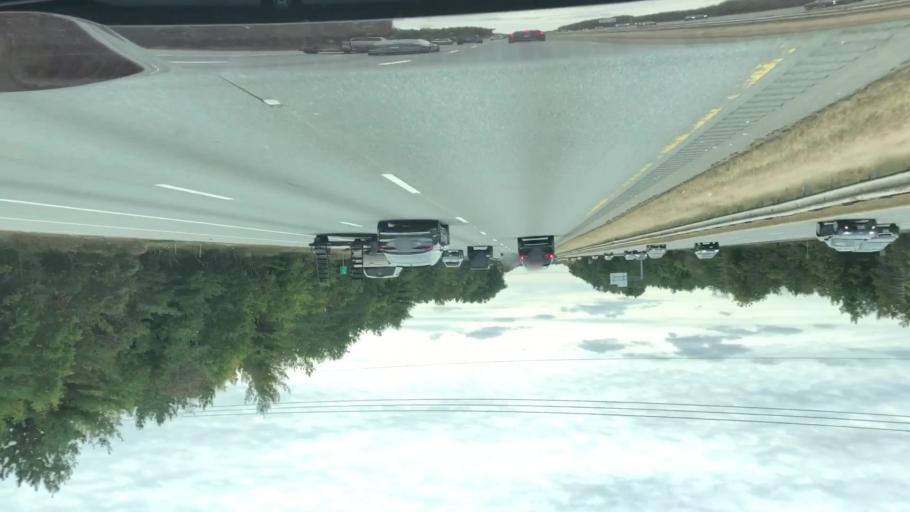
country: US
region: Massachusetts
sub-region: Essex County
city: Andover
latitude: 42.6105
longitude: -71.1737
